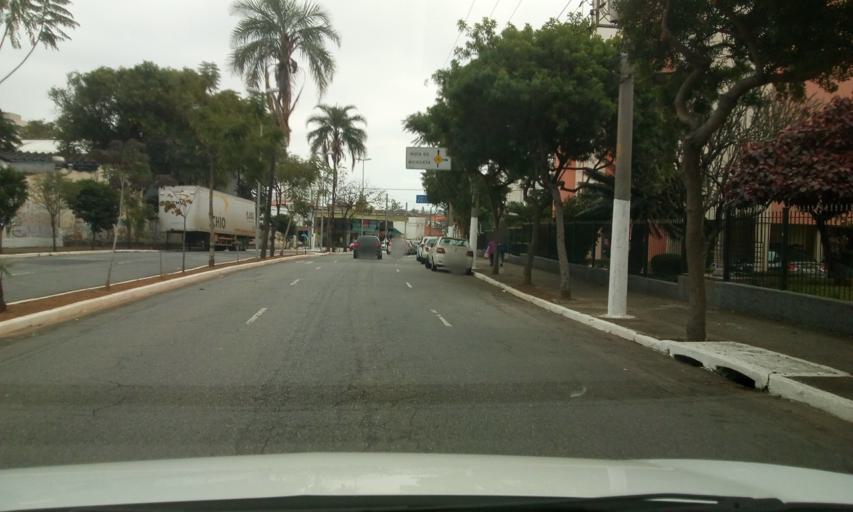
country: BR
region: Sao Paulo
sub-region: Sao Paulo
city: Sao Paulo
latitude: -23.5566
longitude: -46.5874
